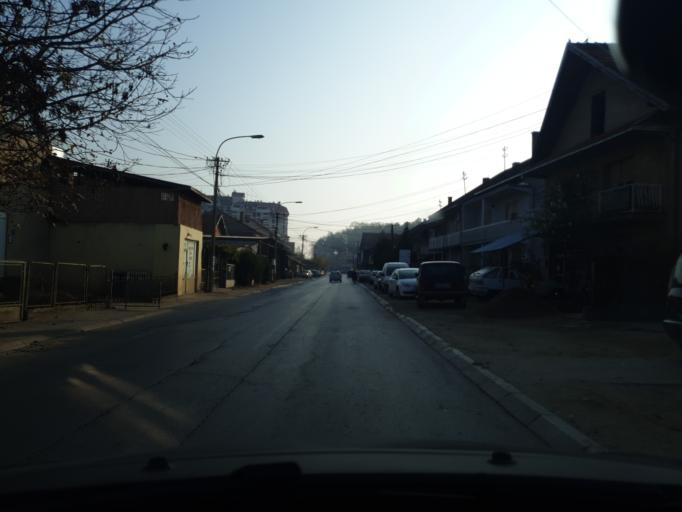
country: RS
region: Central Serbia
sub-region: Jablanicki Okrug
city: Leskovac
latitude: 42.9947
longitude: 21.9318
